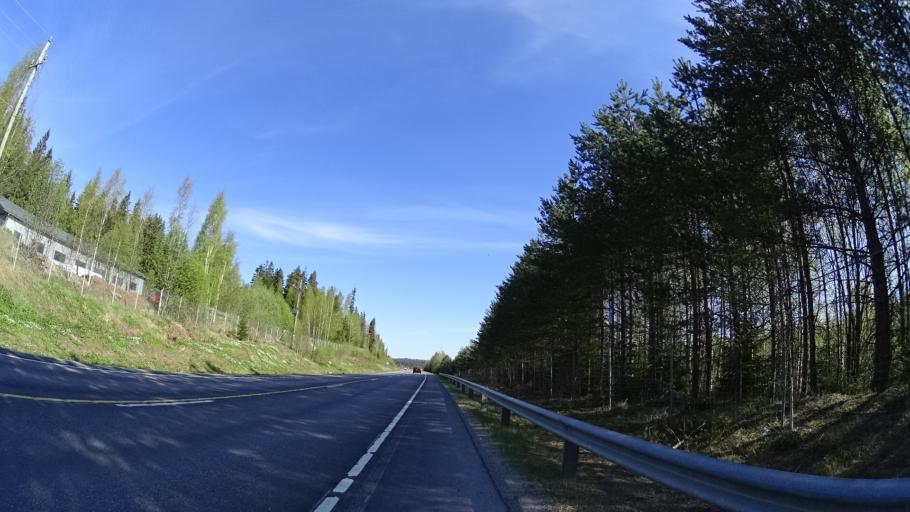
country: FI
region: Uusimaa
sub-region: Helsinki
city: Nurmijaervi
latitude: 60.4151
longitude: 24.8240
